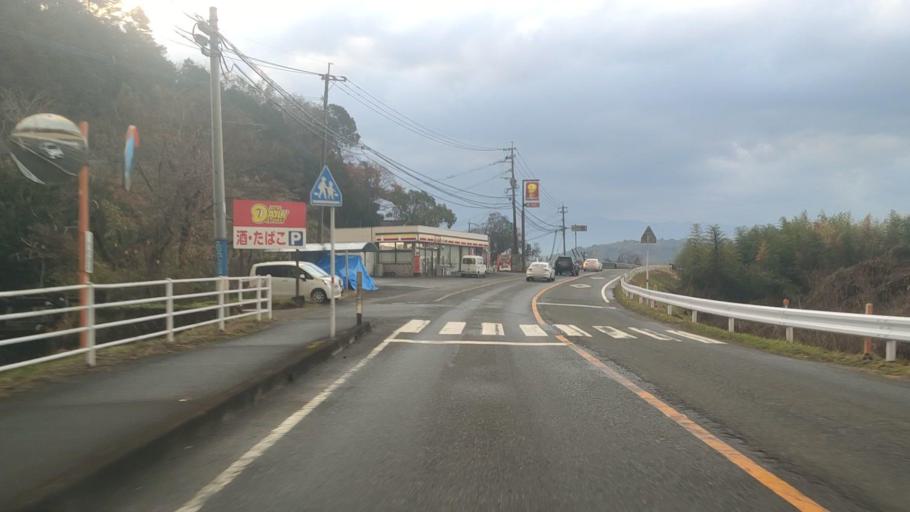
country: JP
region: Kumamoto
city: Uto
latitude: 32.6969
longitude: 130.7878
